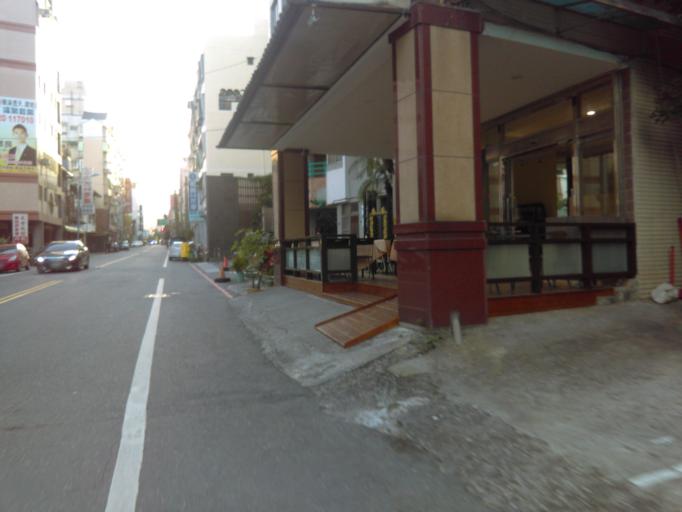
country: TW
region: Taiwan
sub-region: Yilan
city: Yilan
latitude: 24.8273
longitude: 121.7653
